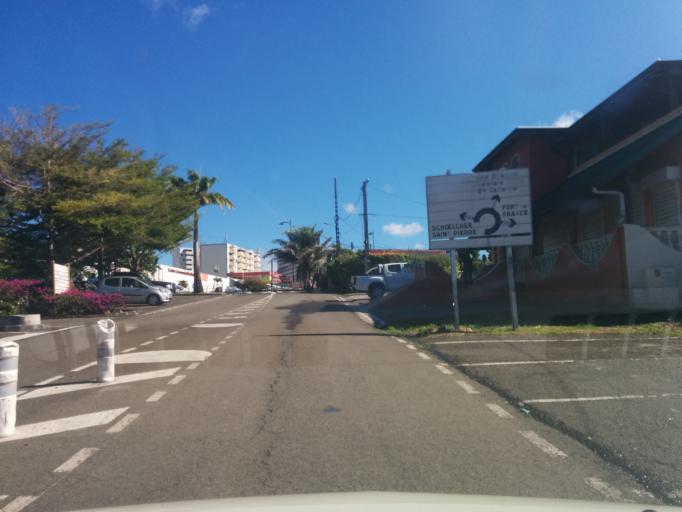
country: MQ
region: Martinique
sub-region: Martinique
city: Fort-de-France
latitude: 14.6065
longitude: -61.0942
